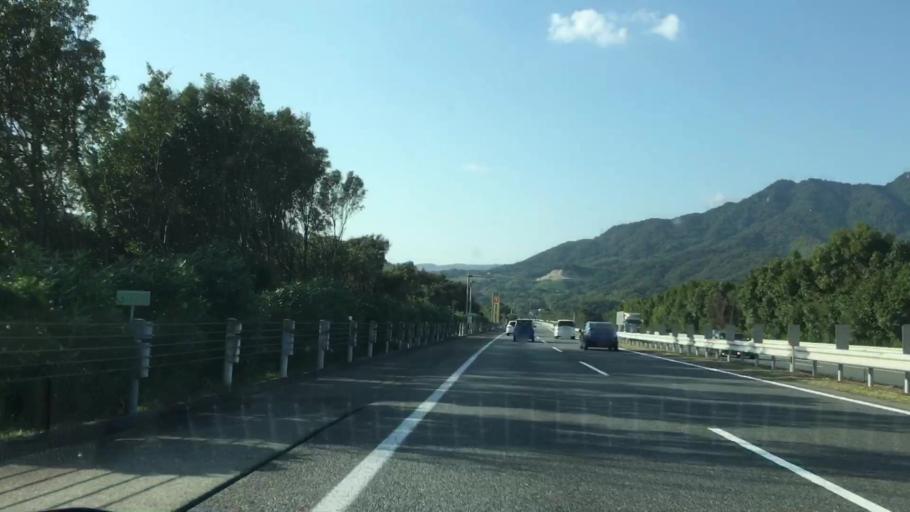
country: JP
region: Yamaguchi
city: Hofu
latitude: 34.0639
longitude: 131.6064
